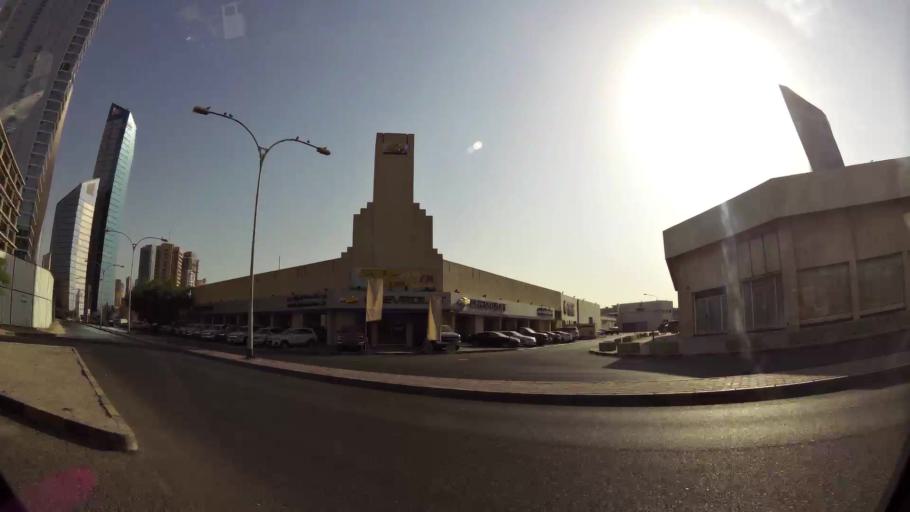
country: KW
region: Al Asimah
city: Kuwait City
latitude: 29.3730
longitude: 47.9893
